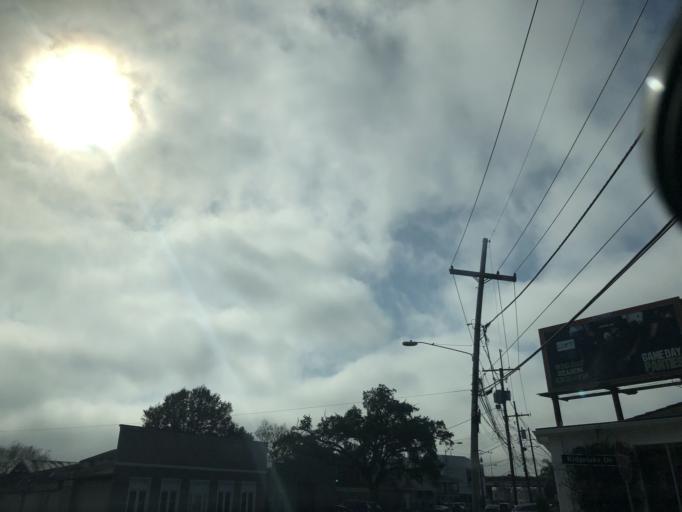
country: US
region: Louisiana
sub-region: Jefferson Parish
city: Metairie
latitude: 29.9775
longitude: -90.1545
